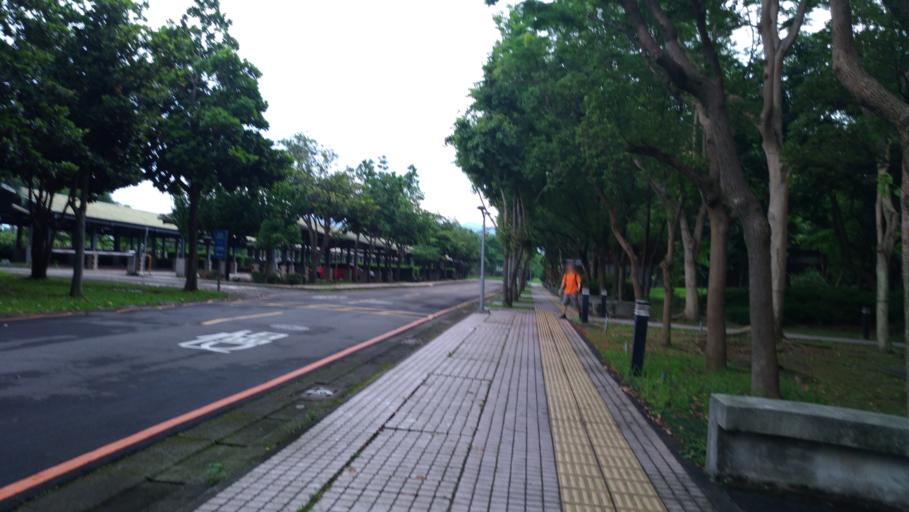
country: TW
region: Taiwan
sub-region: Taoyuan
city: Taoyuan
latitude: 24.9383
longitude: 121.3806
